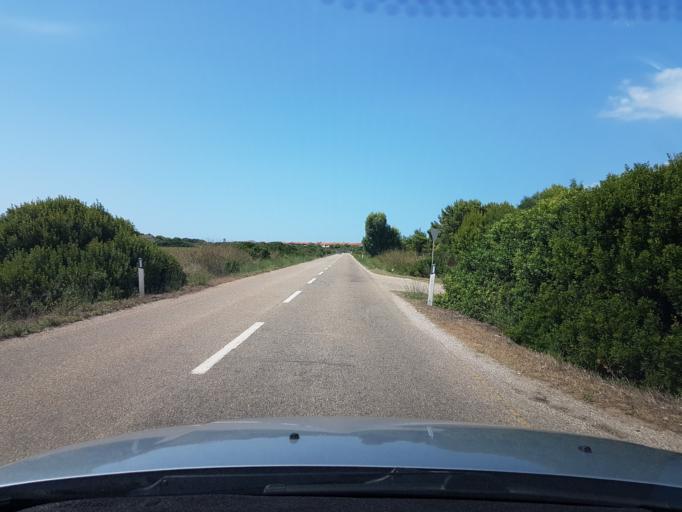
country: IT
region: Sardinia
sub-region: Provincia di Oristano
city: Riola Sardo
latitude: 40.0361
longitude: 8.4208
